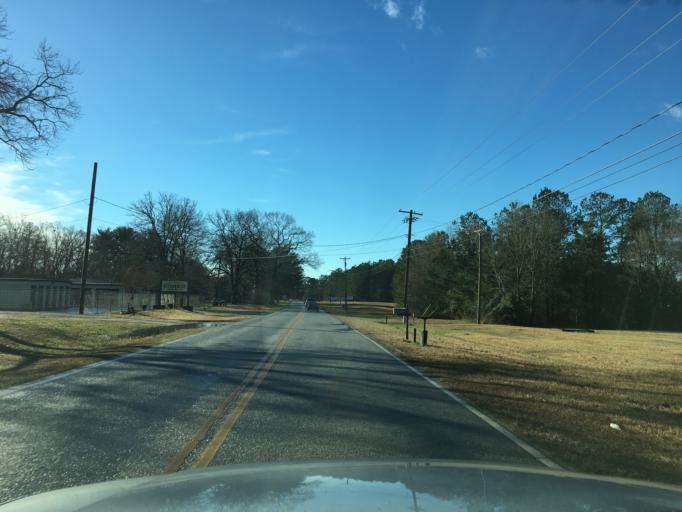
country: US
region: South Carolina
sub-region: Spartanburg County
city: Cowpens
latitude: 35.0120
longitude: -81.8728
